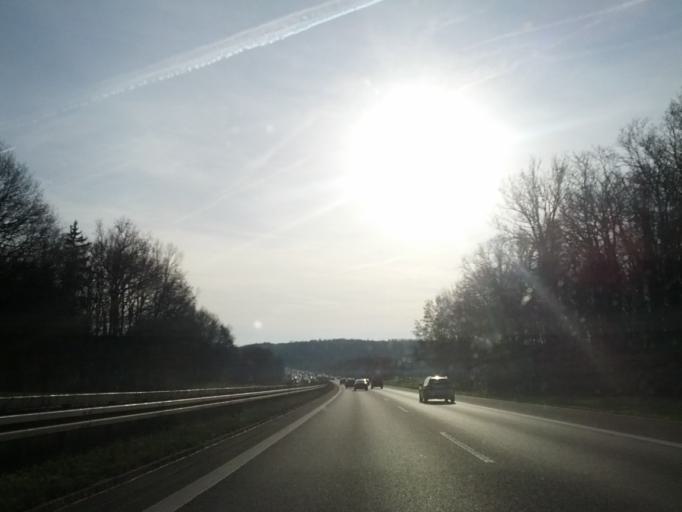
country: DE
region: Bavaria
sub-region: Regierungsbezirk Unterfranken
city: Rimpar
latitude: 49.8658
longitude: 9.9923
